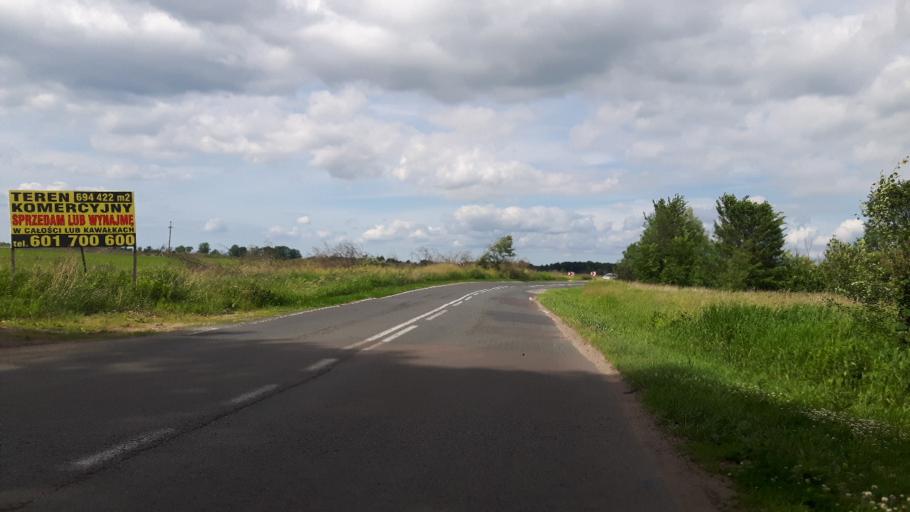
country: PL
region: West Pomeranian Voivodeship
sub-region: Szczecin
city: Szczecin
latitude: 53.4162
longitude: 14.7035
